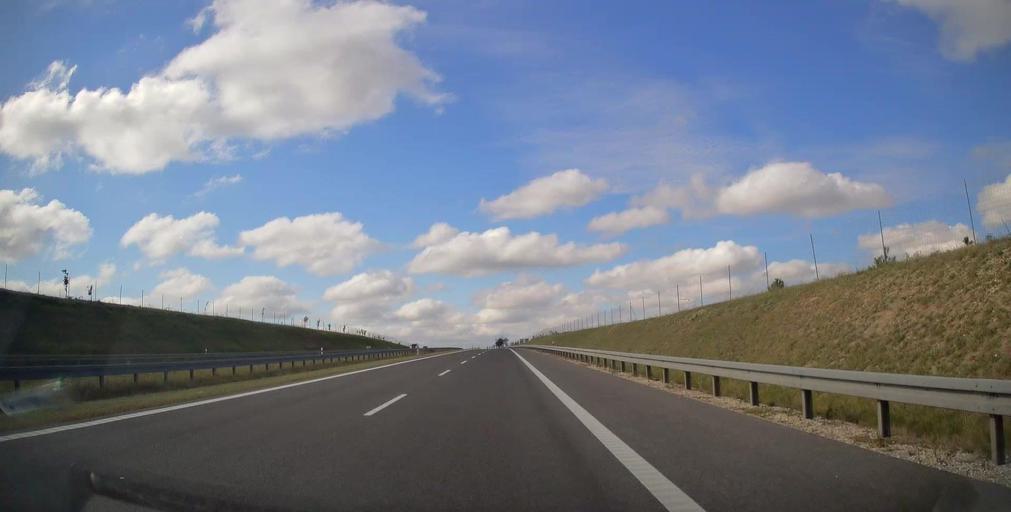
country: PL
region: Swietokrzyskie
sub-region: Powiat jedrzejowski
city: Wodzislaw
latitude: 50.5097
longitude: 20.1913
